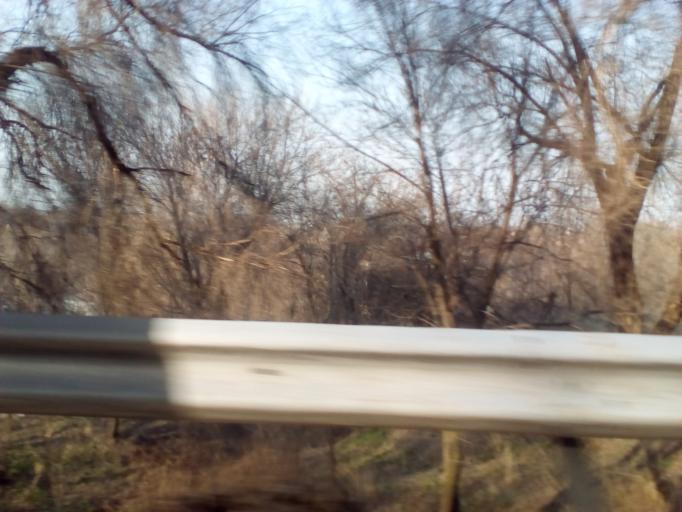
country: KZ
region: Almaty Oblysy
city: Burunday
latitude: 43.1647
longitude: 76.5493
